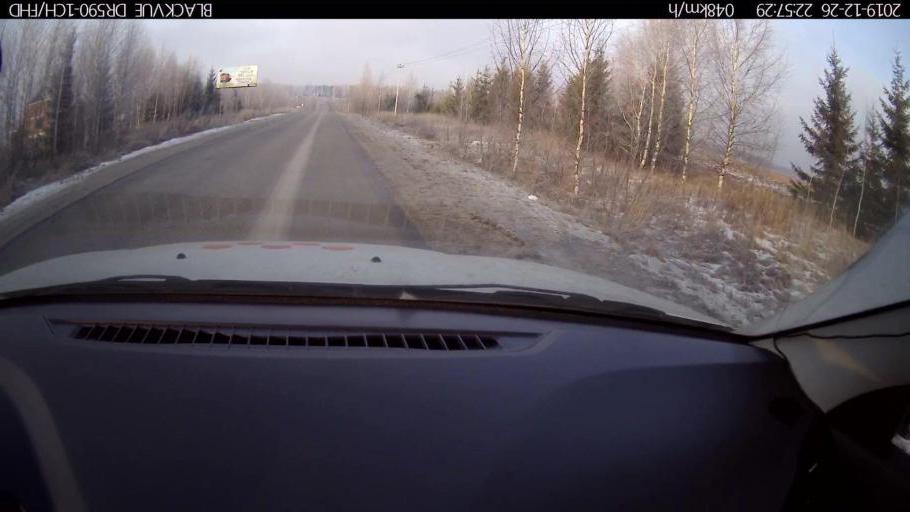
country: RU
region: Nizjnij Novgorod
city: Burevestnik
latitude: 56.1509
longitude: 43.7155
